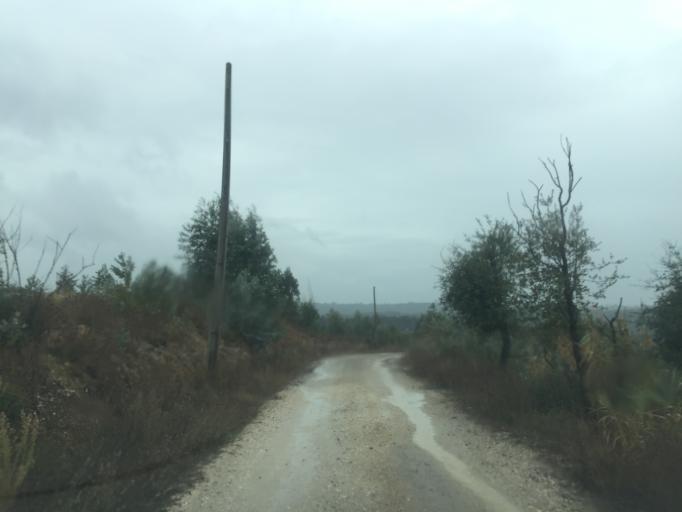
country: PT
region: Coimbra
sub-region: Figueira da Foz
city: Lavos
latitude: 40.0763
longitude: -8.7877
